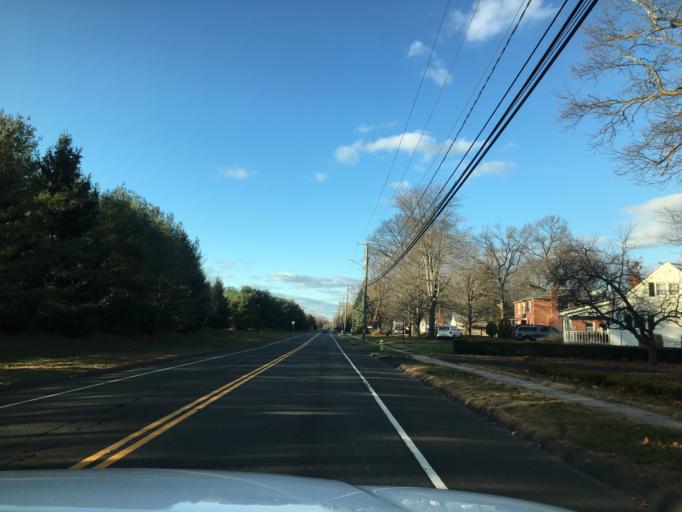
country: US
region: Connecticut
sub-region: Hartford County
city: Windsor Locks
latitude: 41.9118
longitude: -72.6582
